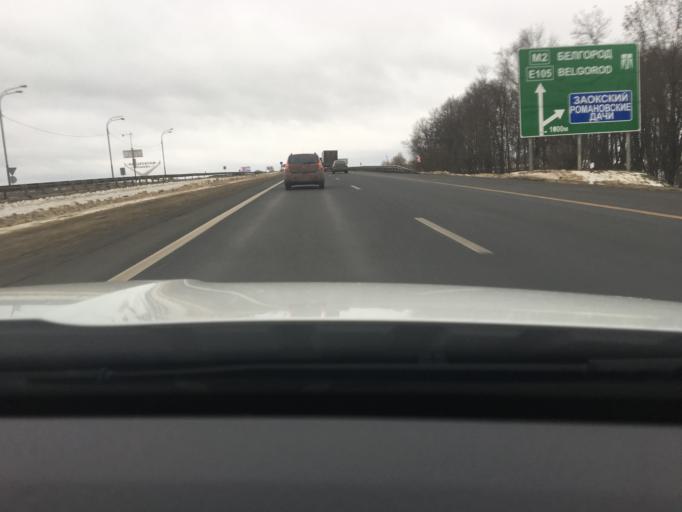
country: RU
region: Moskovskaya
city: Serpukhov
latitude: 54.8467
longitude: 37.4662
